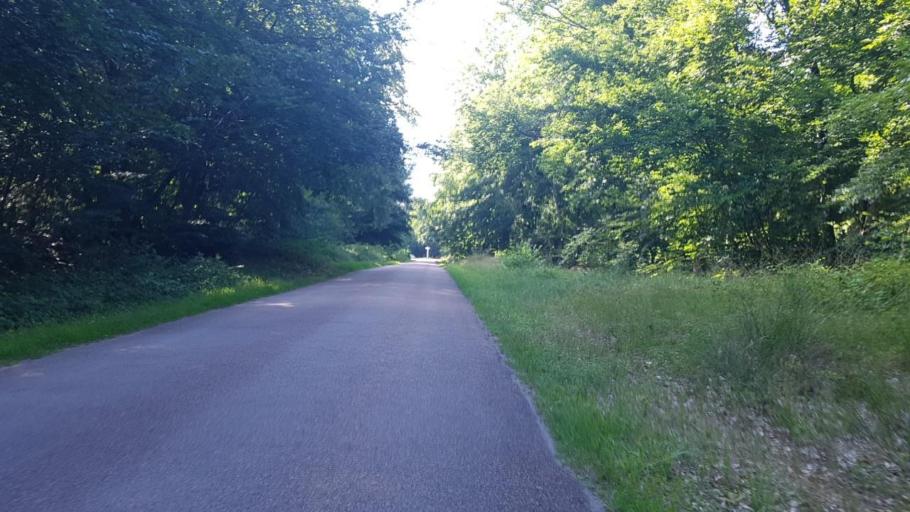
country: FR
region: Picardie
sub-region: Departement de l'Oise
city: Ver-sur-Launette
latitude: 49.1502
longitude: 2.6414
